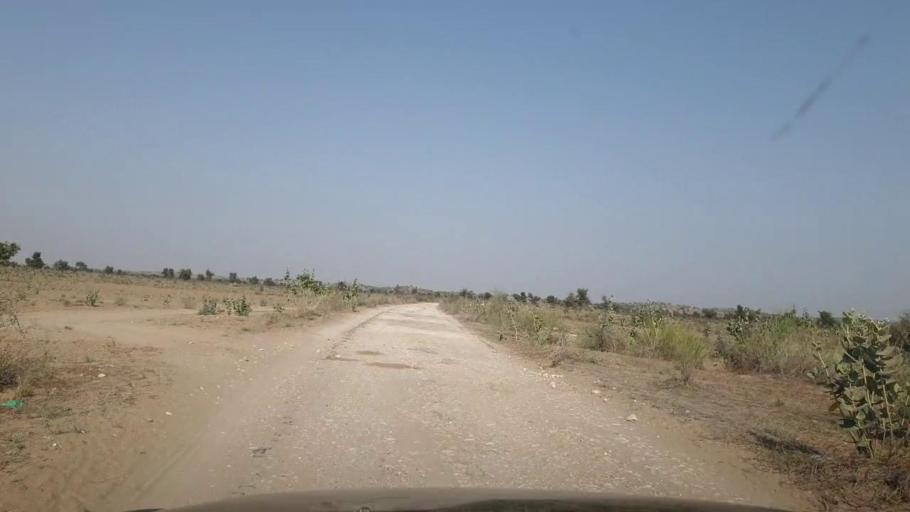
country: PK
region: Sindh
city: Islamkot
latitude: 25.0989
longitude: 70.4013
